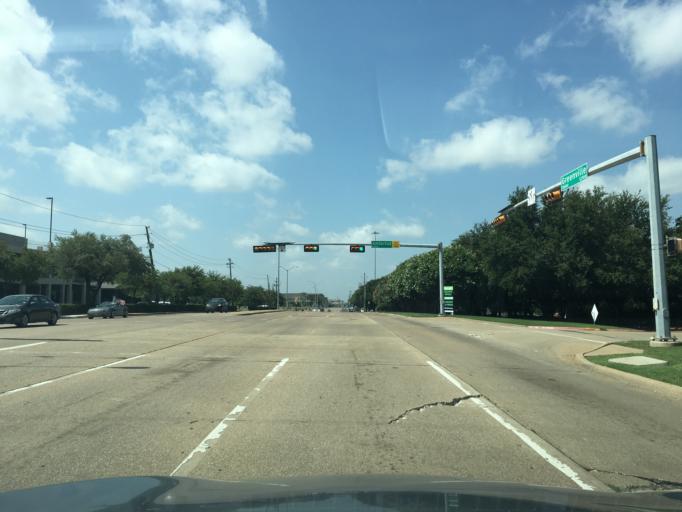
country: US
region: Texas
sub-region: Dallas County
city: Richardson
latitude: 32.9200
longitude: -96.7420
